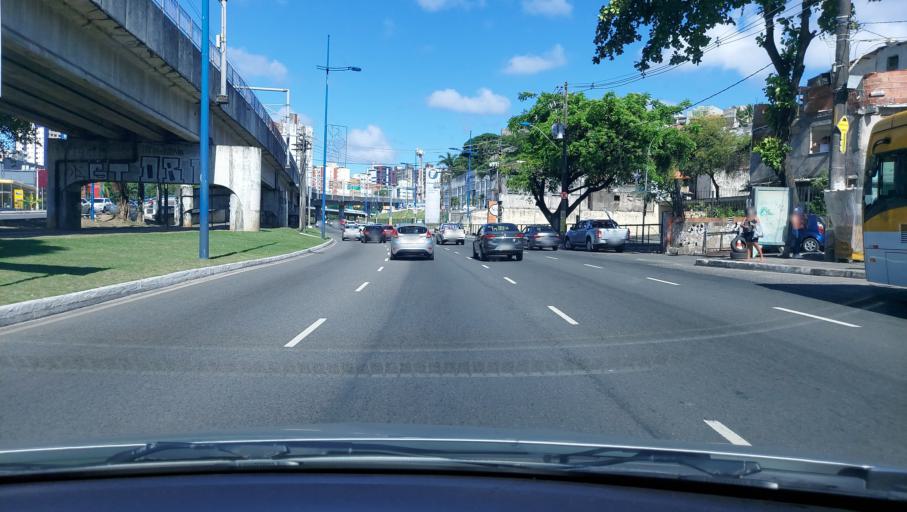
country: BR
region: Bahia
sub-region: Salvador
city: Salvador
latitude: -12.9833
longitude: -38.4916
